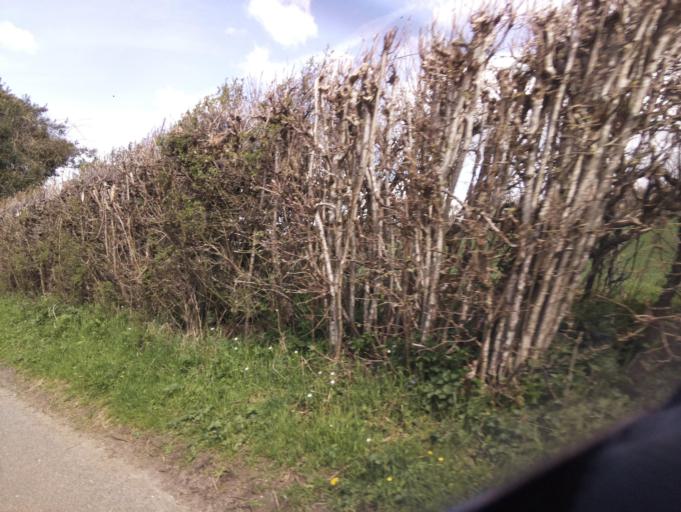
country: GB
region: England
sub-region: West Berkshire
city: Kintbury
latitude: 51.3129
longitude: -1.4598
